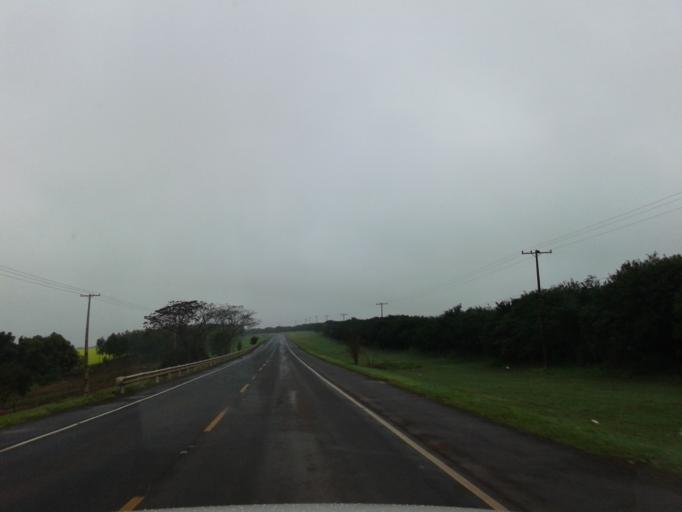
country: PY
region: Alto Parana
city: Naranjal
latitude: -26.1401
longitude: -55.1620
